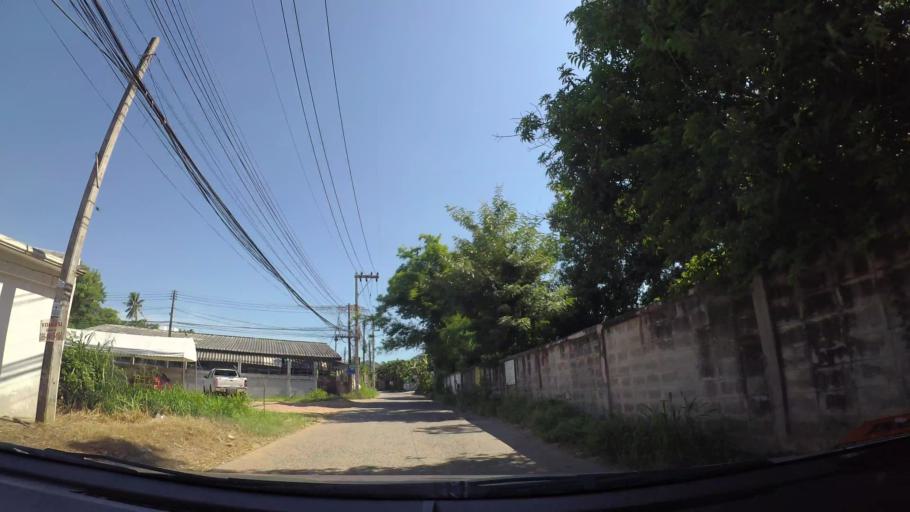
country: TH
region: Chon Buri
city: Si Racha
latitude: 13.1581
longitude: 100.9345
